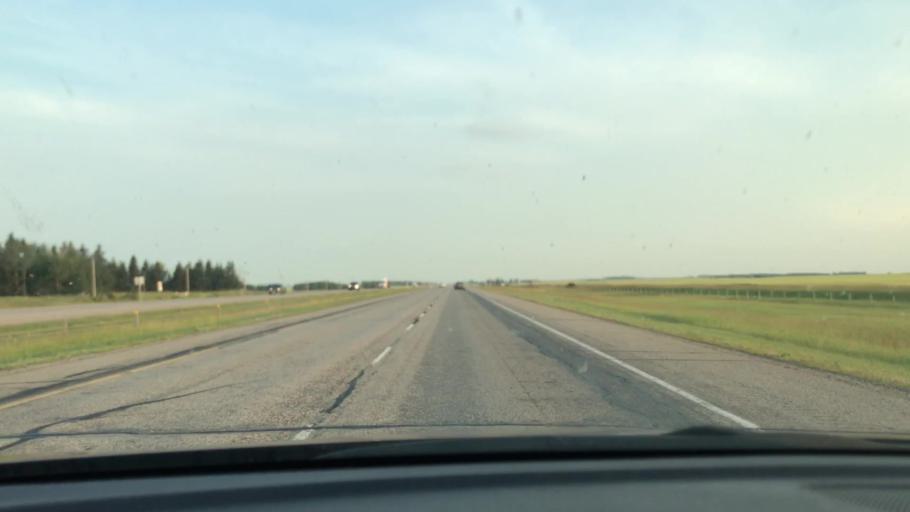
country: CA
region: Alberta
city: Olds
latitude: 51.8602
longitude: -114.0256
